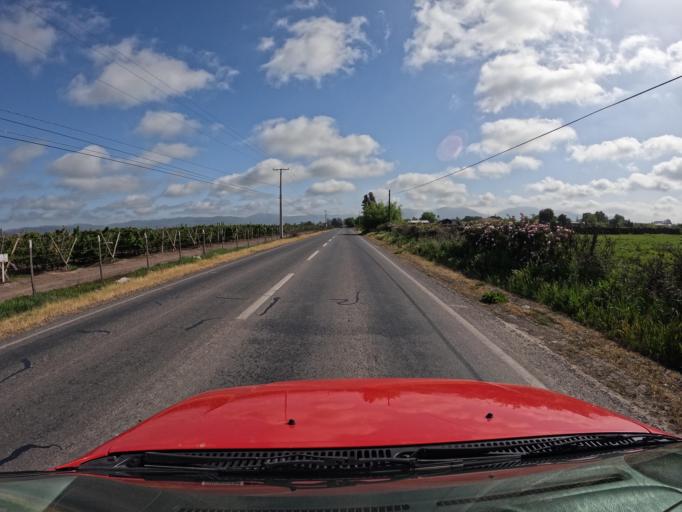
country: CL
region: Maule
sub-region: Provincia de Curico
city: Rauco
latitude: -34.8977
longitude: -71.2735
